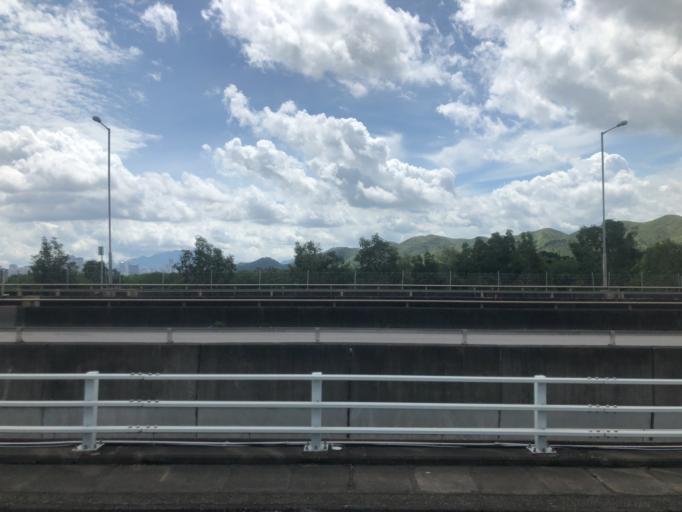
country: CN
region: Guangdong
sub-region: Shenzhen
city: Shenzhen
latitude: 22.5163
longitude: 114.0710
